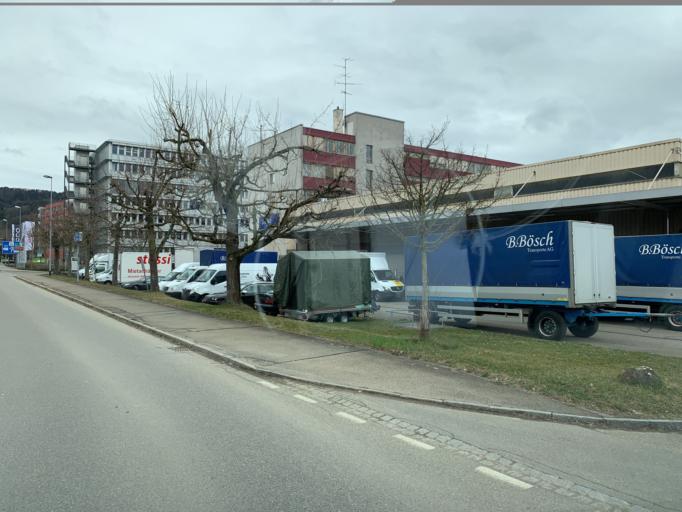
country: CH
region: Aargau
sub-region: Bezirk Baden
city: Spreitenbach
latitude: 47.4255
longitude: 8.3714
